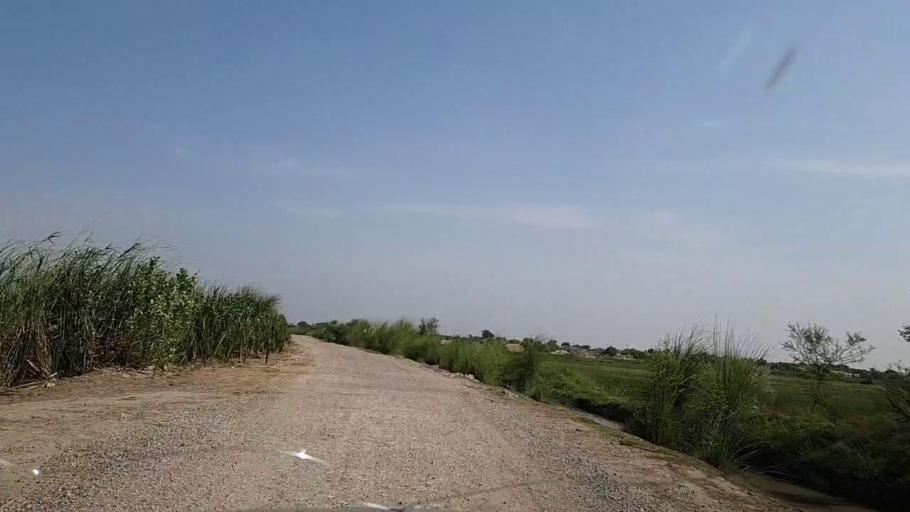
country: PK
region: Sindh
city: Khanpur
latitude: 27.7181
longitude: 69.3610
